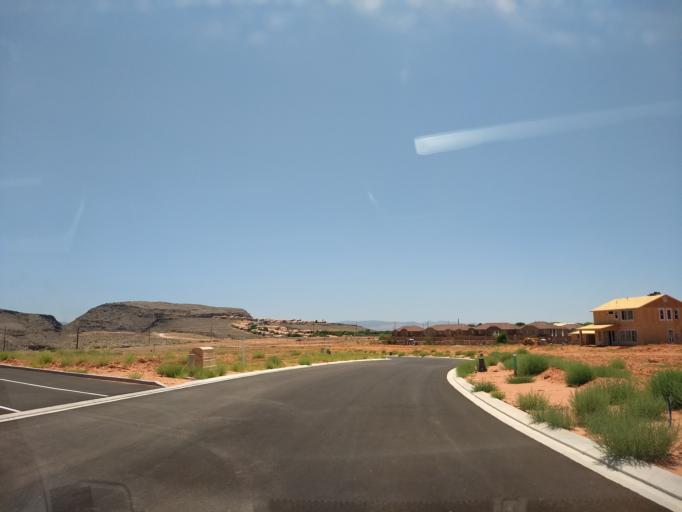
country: US
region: Utah
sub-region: Washington County
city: Washington
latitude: 37.1371
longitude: -113.4820
